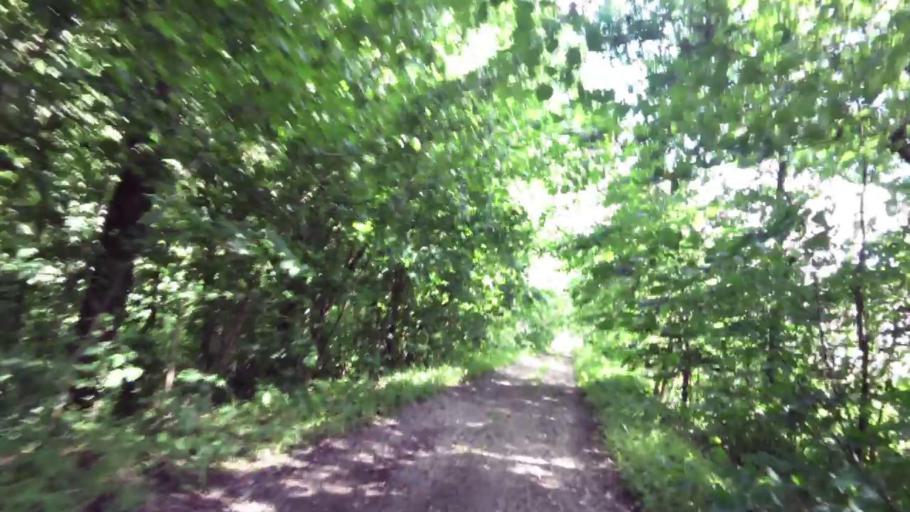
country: PL
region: West Pomeranian Voivodeship
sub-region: Powiat slawienski
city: Slawno
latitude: 54.5040
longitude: 16.7047
